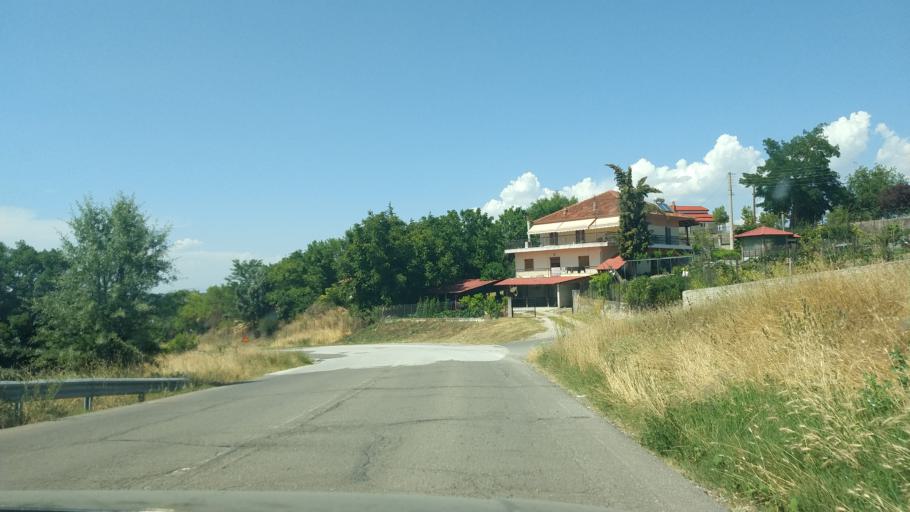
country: GR
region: West Macedonia
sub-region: Nomos Grevenon
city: Grevena
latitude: 40.0388
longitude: 21.4814
